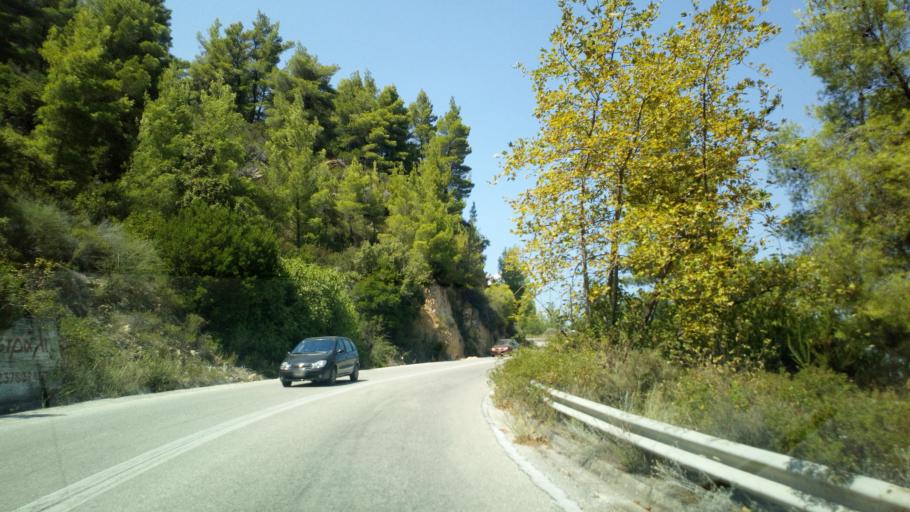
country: GR
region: Central Macedonia
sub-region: Nomos Chalkidikis
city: Sarti
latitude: 40.1574
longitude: 23.8932
